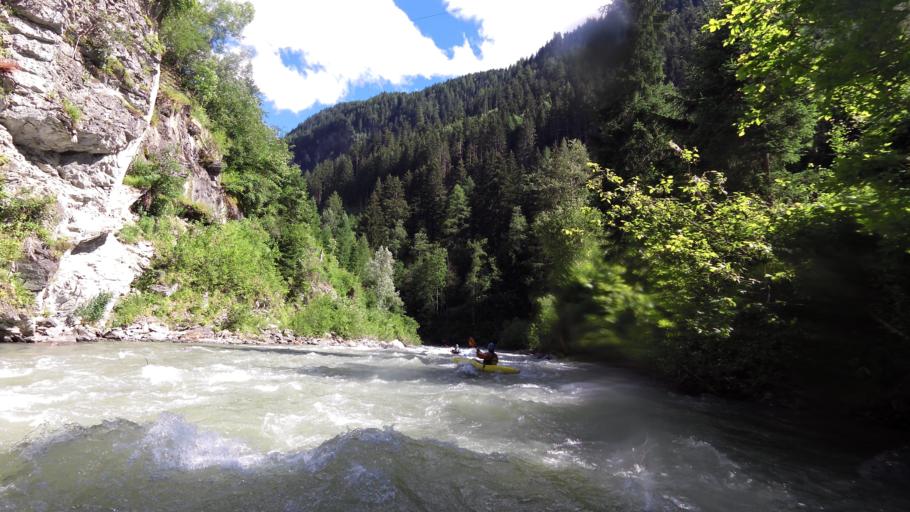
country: AT
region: Tyrol
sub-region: Politischer Bezirk Landeck
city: Strengen
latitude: 47.1248
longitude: 10.4620
